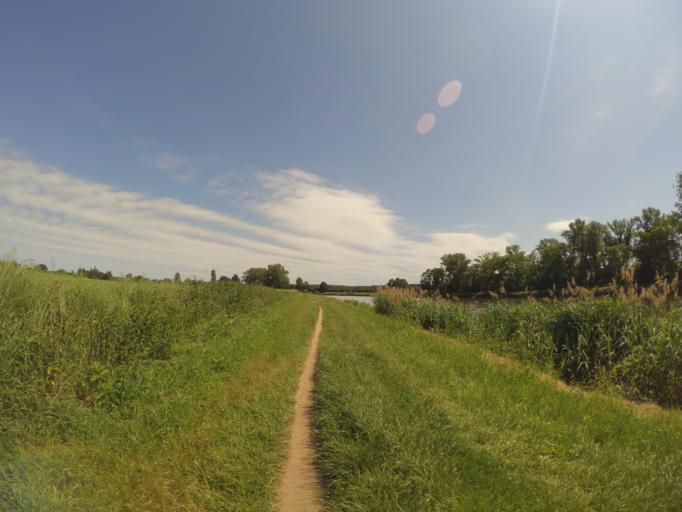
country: CZ
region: Central Bohemia
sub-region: Okres Nymburk
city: Sadska
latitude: 50.1654
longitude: 14.9568
